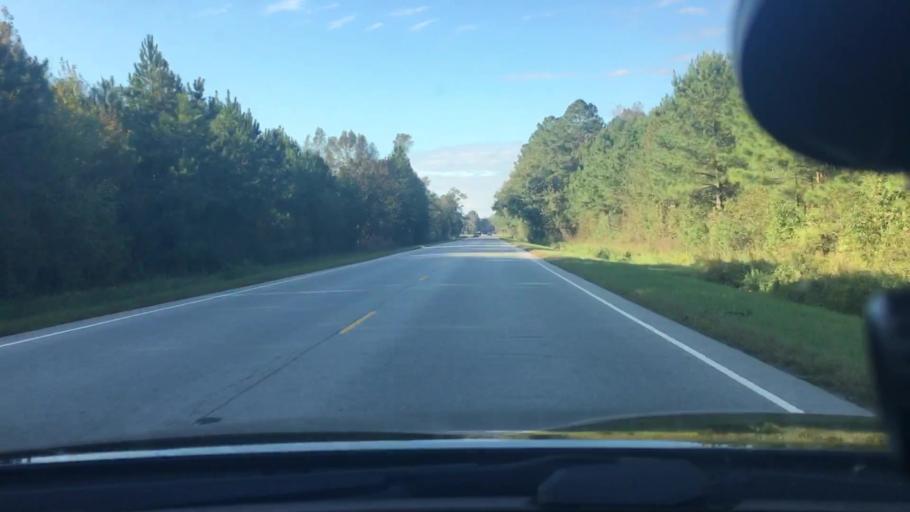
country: US
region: North Carolina
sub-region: Craven County
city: Vanceboro
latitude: 35.3228
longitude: -77.1463
